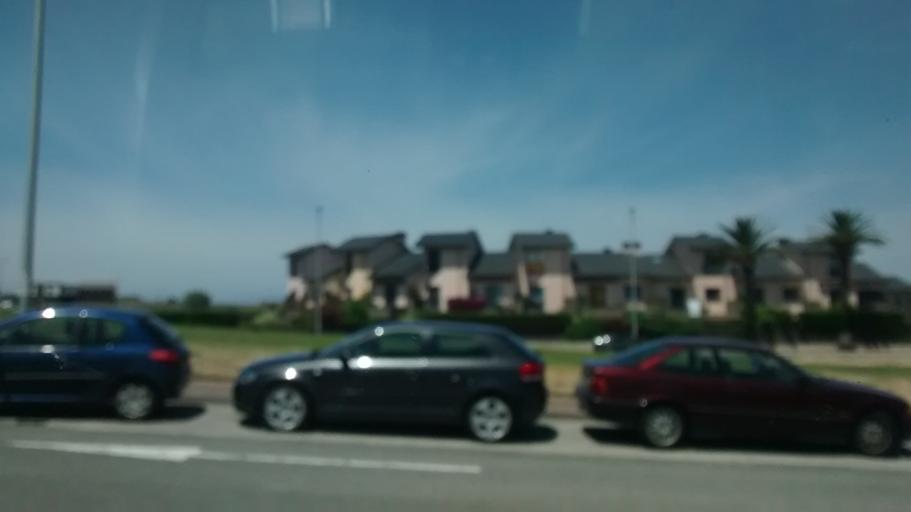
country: ES
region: Cantabria
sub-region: Provincia de Cantabria
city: Santander
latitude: 43.4679
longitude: -3.8337
